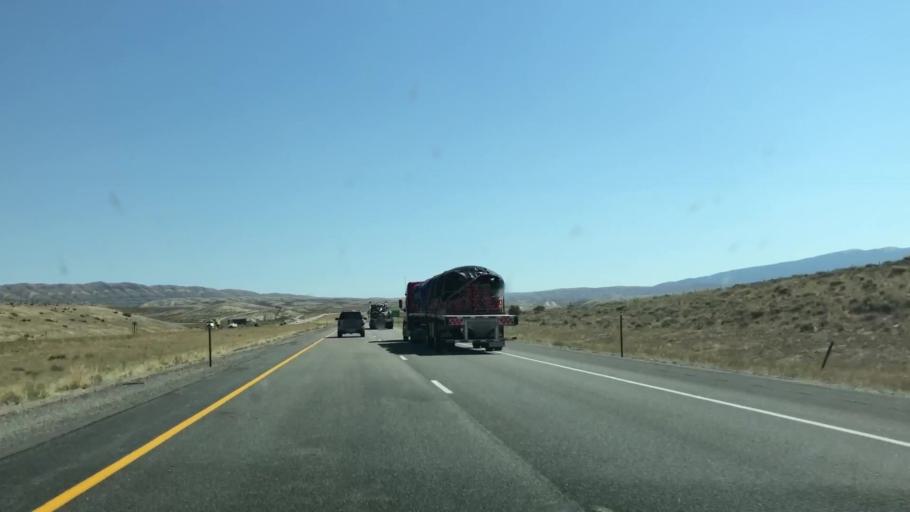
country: US
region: Wyoming
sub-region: Carbon County
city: Saratoga
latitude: 41.7413
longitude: -106.7883
